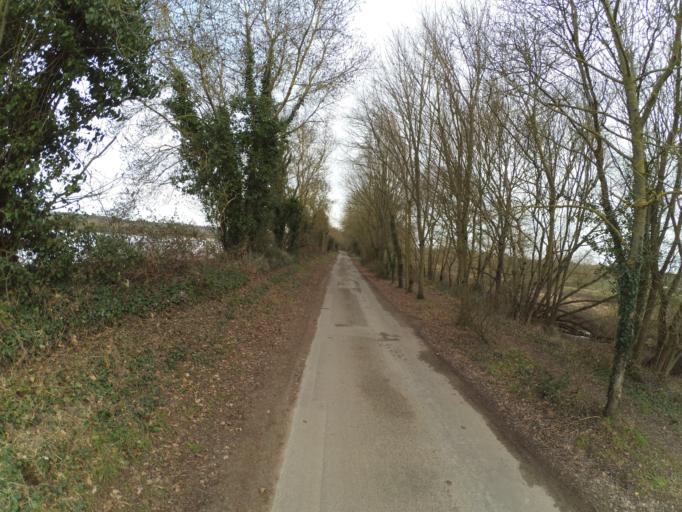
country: FR
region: Pays de la Loire
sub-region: Departement de la Loire-Atlantique
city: Mauves-sur-Loire
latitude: 47.2842
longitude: -1.4025
